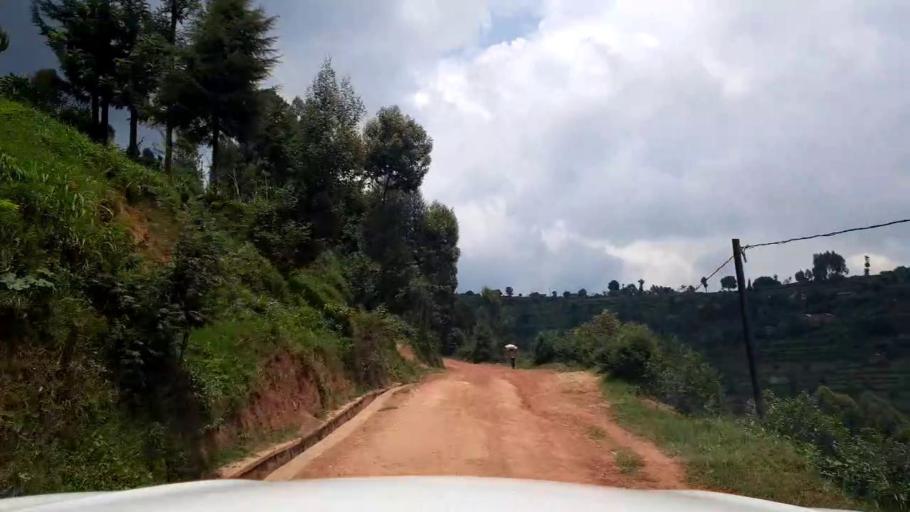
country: RW
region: Northern Province
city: Byumba
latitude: -1.4869
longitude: 29.9258
